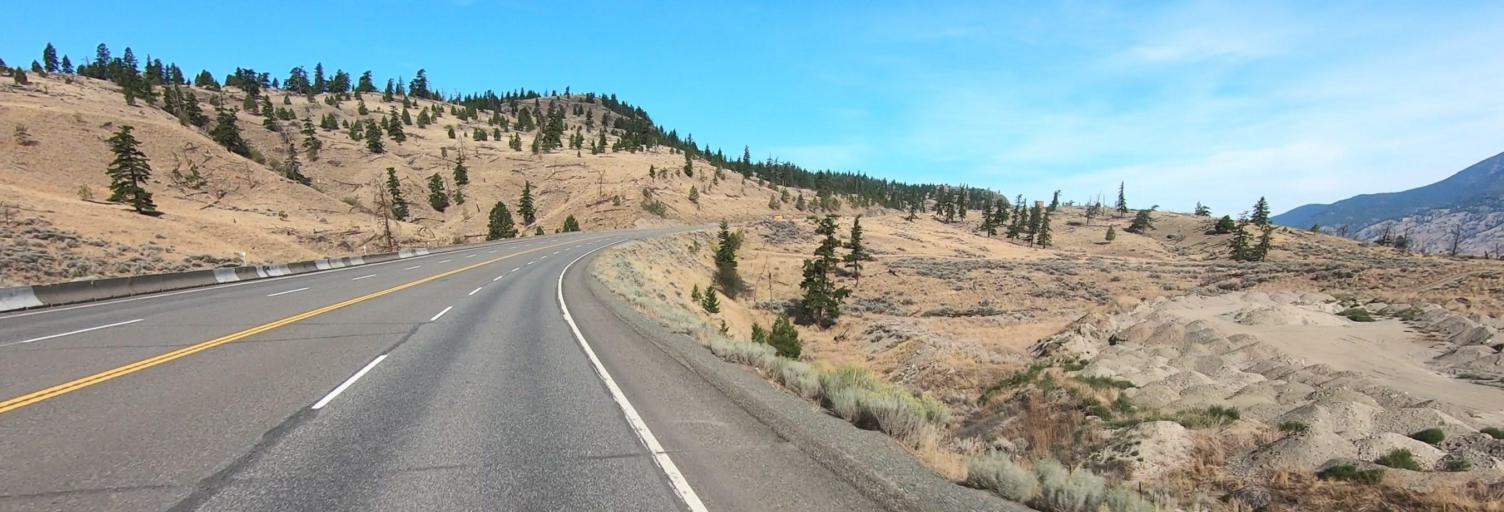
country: CA
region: British Columbia
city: Logan Lake
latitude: 50.7392
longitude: -120.7160
